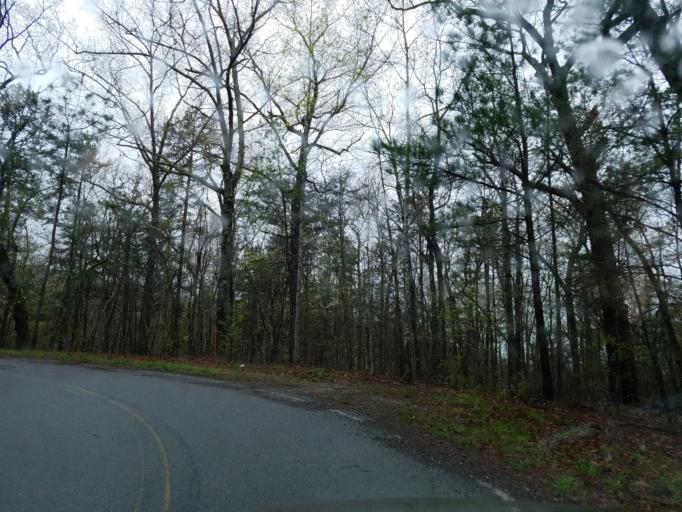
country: US
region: Georgia
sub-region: Fannin County
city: Blue Ridge
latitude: 34.8532
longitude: -84.2322
